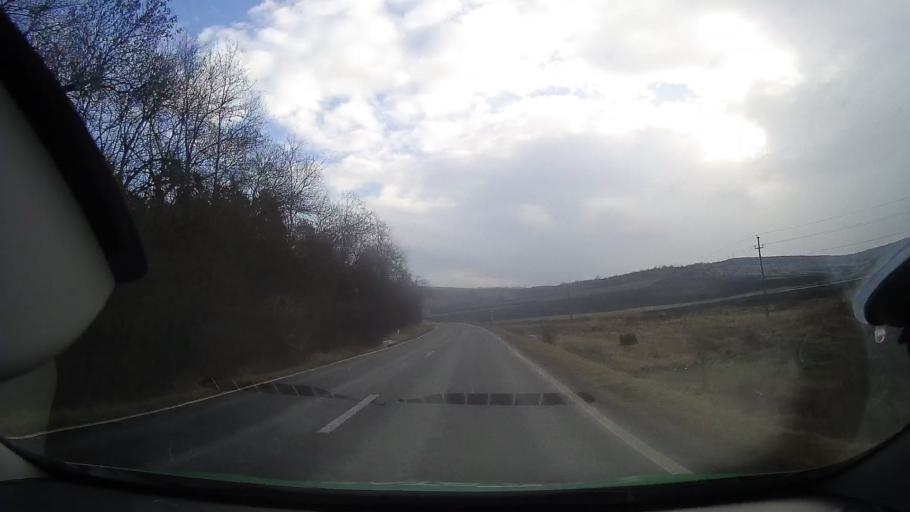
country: RO
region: Mures
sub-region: Comuna Cucerdea
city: Cucerdea
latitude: 46.3665
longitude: 24.2657
